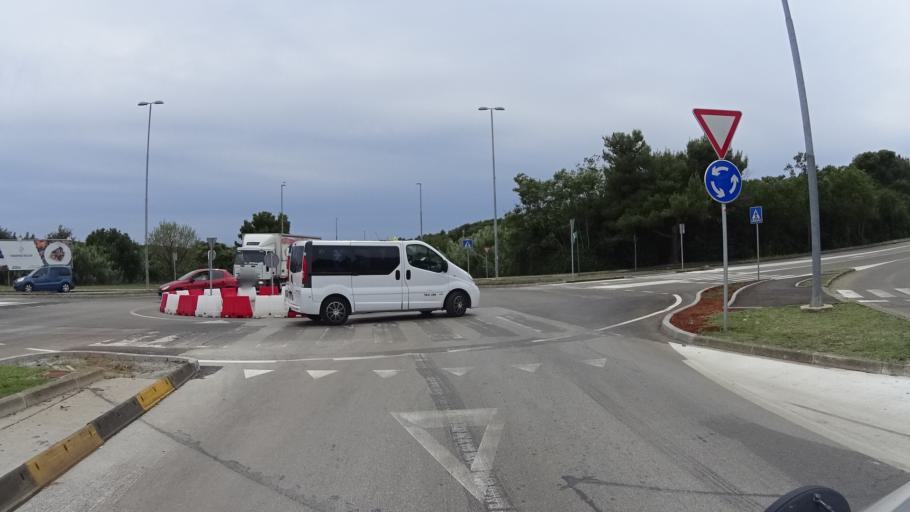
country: HR
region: Istarska
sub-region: Grad Pula
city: Pula
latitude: 44.8483
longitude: 13.8411
